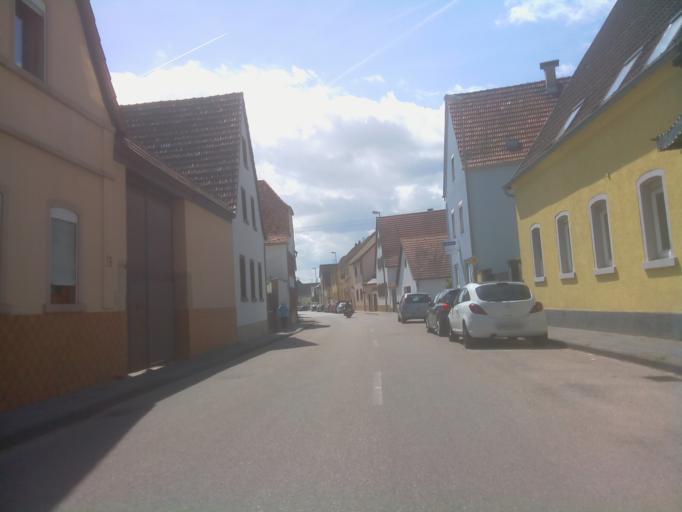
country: DE
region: Rheinland-Pfalz
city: Neuhofen
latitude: 49.4206
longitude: 8.4298
